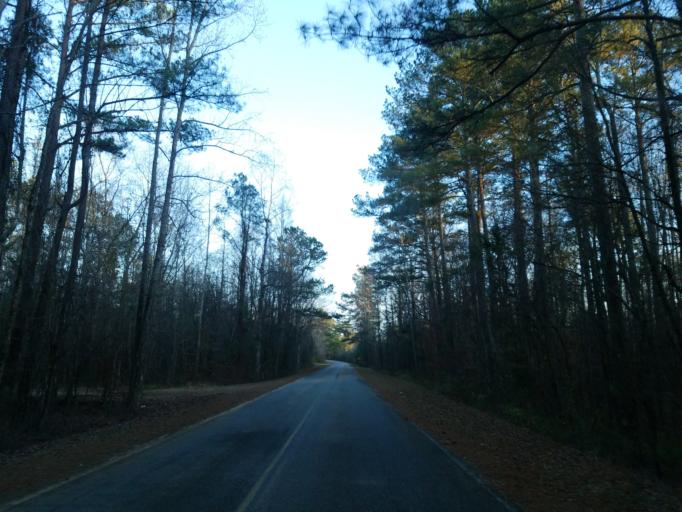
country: US
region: Mississippi
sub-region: Lauderdale County
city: Meridian
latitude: 32.2666
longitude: -88.7856
